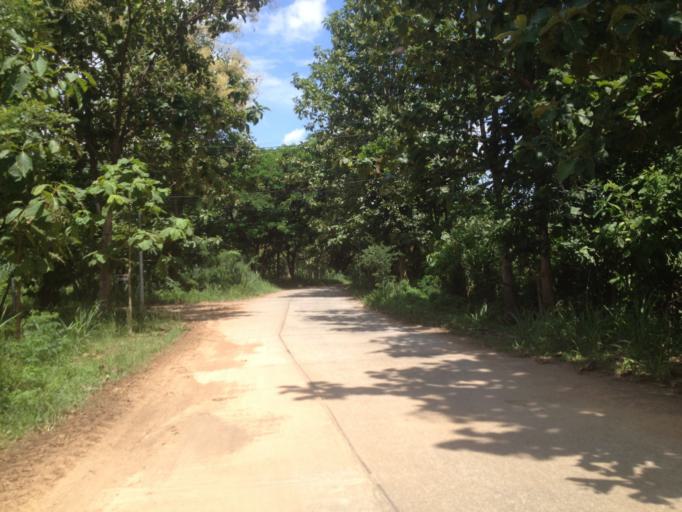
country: TH
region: Chiang Mai
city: Chiang Mai
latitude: 18.7662
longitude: 98.9298
